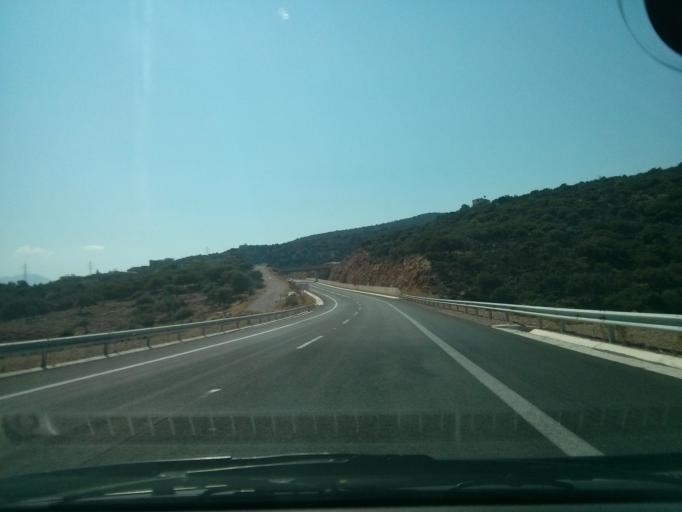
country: GR
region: Crete
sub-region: Nomos Lasithiou
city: Agios Nikolaos
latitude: 35.1671
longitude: 25.7032
